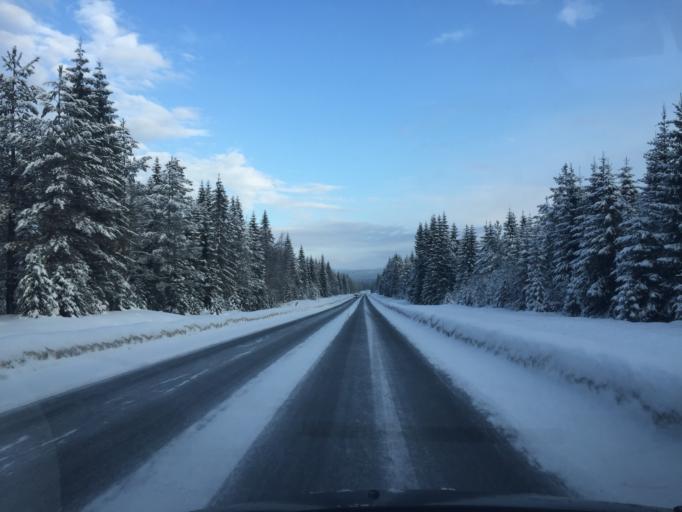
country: NO
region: Hedmark
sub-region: Trysil
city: Innbygda
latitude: 61.0739
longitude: 11.9741
